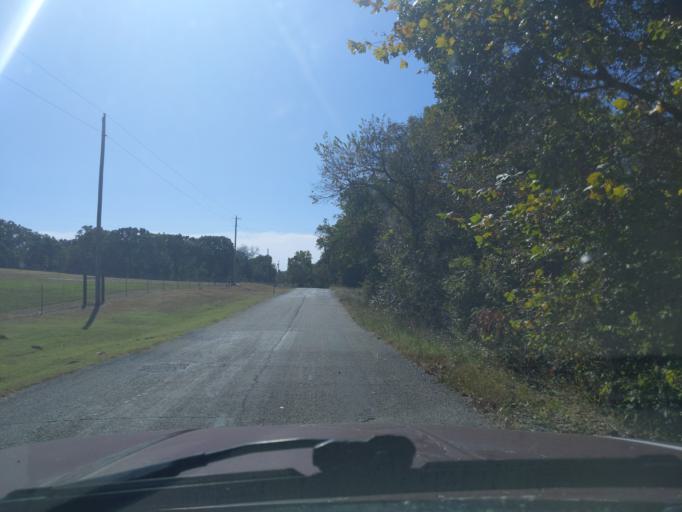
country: US
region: Oklahoma
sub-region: Creek County
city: Bristow
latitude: 35.7096
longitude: -96.4055
